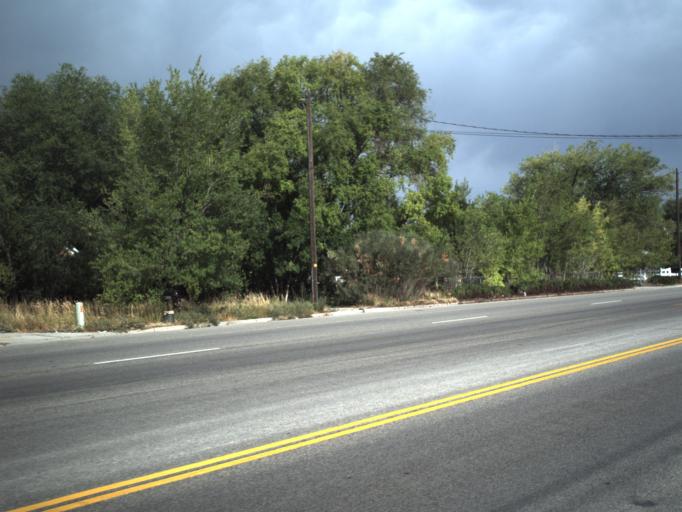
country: US
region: Utah
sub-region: Weber County
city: Harrisville
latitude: 41.2701
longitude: -111.9693
